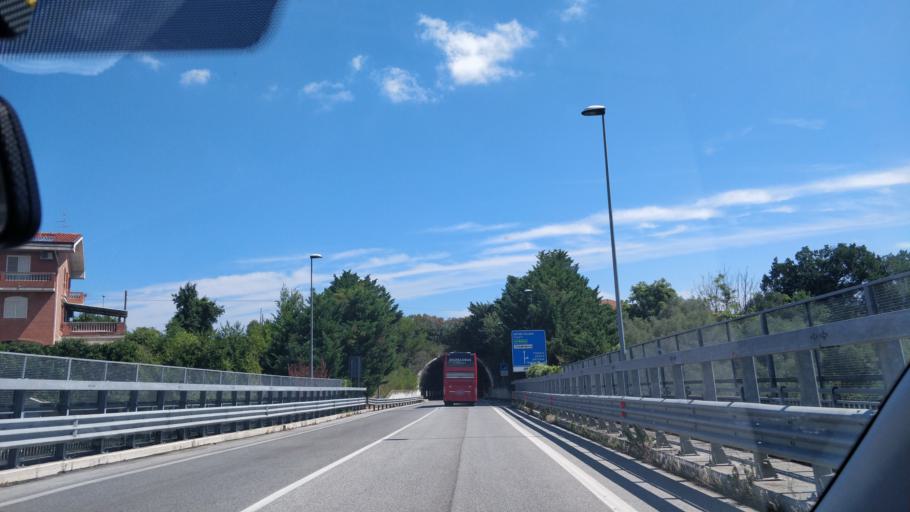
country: IT
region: Abruzzo
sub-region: Provincia di Chieti
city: Francavilla al Mare
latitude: 42.4003
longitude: 14.2973
